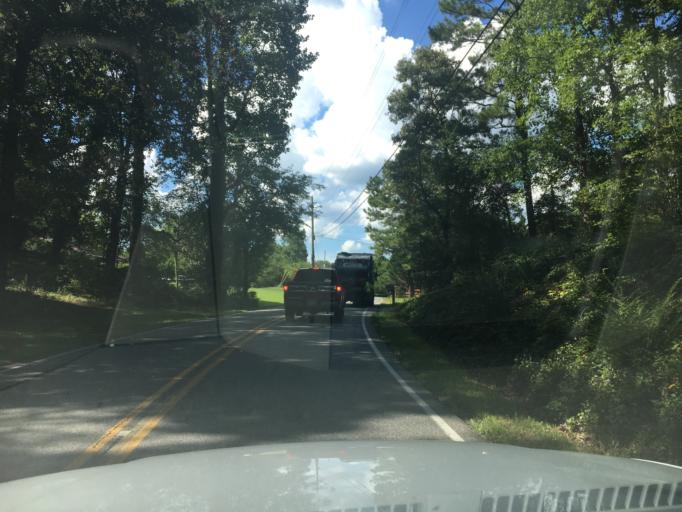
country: US
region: Georgia
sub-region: Cherokee County
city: Holly Springs
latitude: 34.1463
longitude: -84.4643
